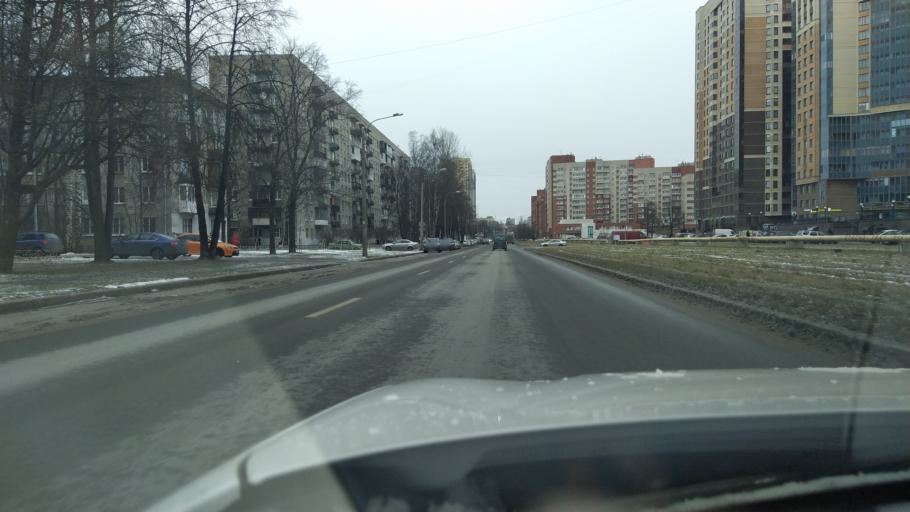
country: RU
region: Leningrad
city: Akademicheskoe
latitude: 60.0049
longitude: 30.3997
